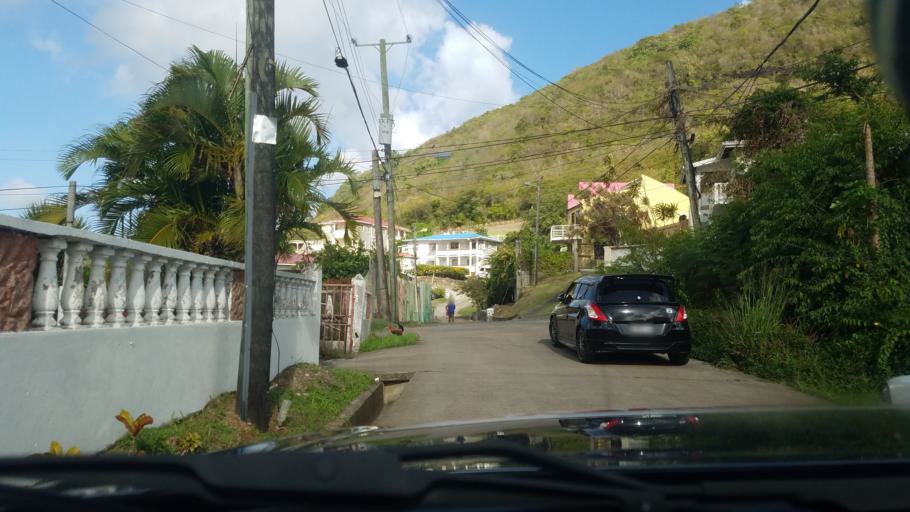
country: LC
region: Gros-Islet
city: Gros Islet
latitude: 14.0653
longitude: -60.9582
